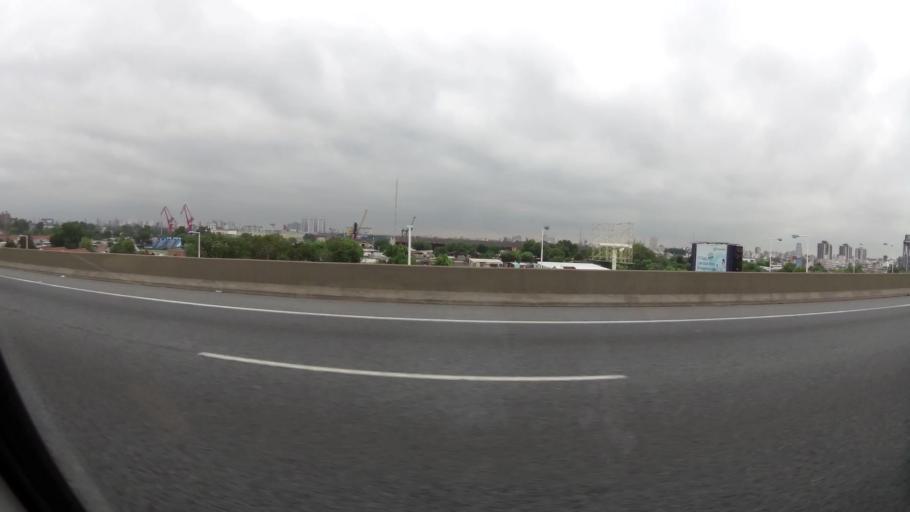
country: AR
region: Buenos Aires
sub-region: Partido de Avellaneda
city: Avellaneda
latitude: -34.6412
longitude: -58.3513
